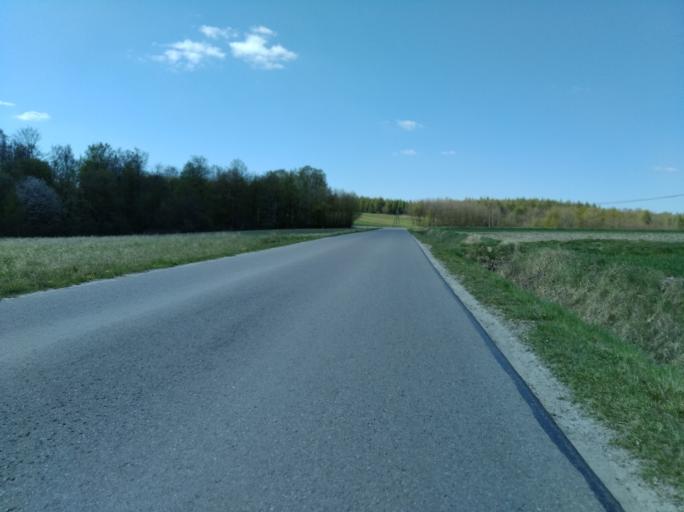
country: PL
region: Subcarpathian Voivodeship
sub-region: Powiat strzyzowski
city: Wisniowa
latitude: 49.9032
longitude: 21.6708
